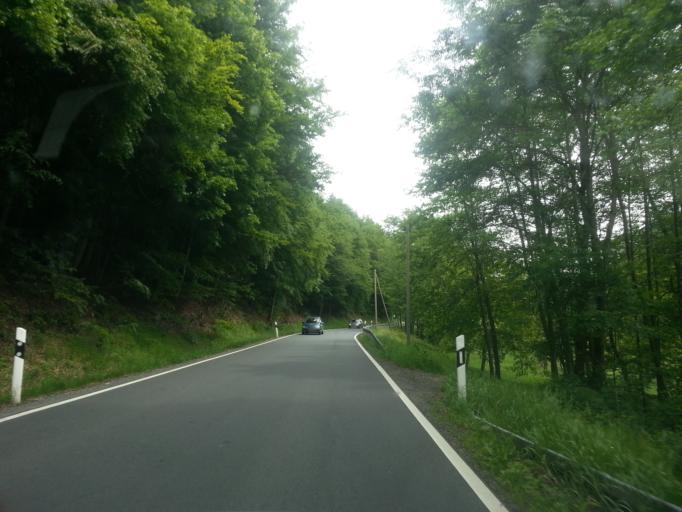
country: DE
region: Hesse
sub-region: Regierungsbezirk Darmstadt
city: Seeheim-Jugenheim
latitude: 49.7324
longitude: 8.6738
